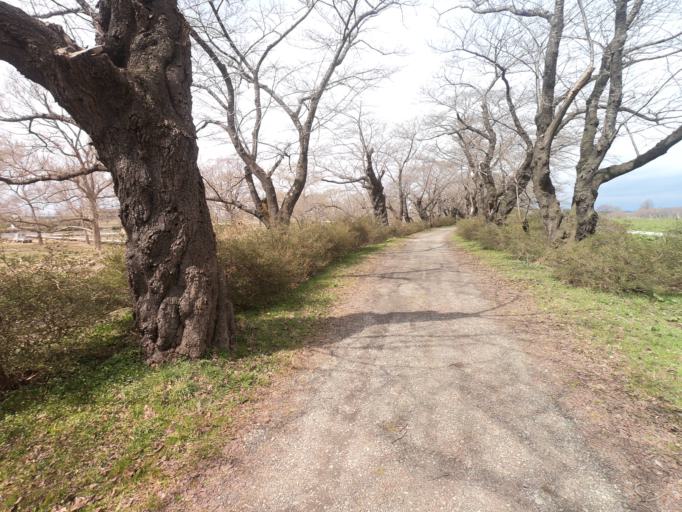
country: JP
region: Iwate
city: Kitakami
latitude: 39.2746
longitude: 141.1267
